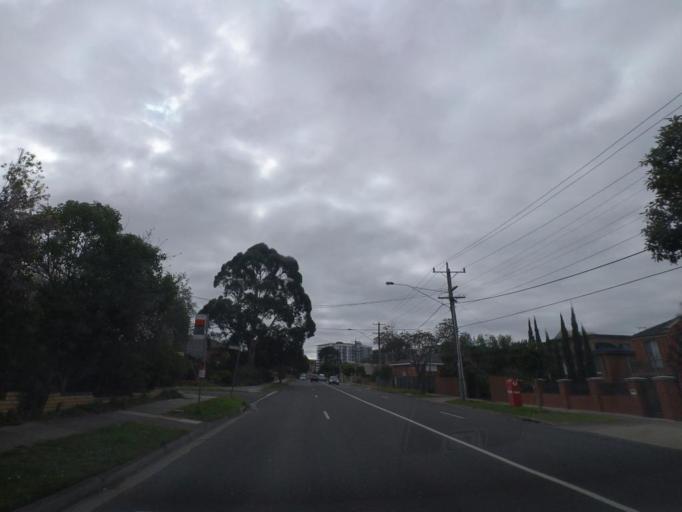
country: AU
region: Victoria
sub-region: Manningham
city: Doncaster
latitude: -37.7918
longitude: 145.1220
